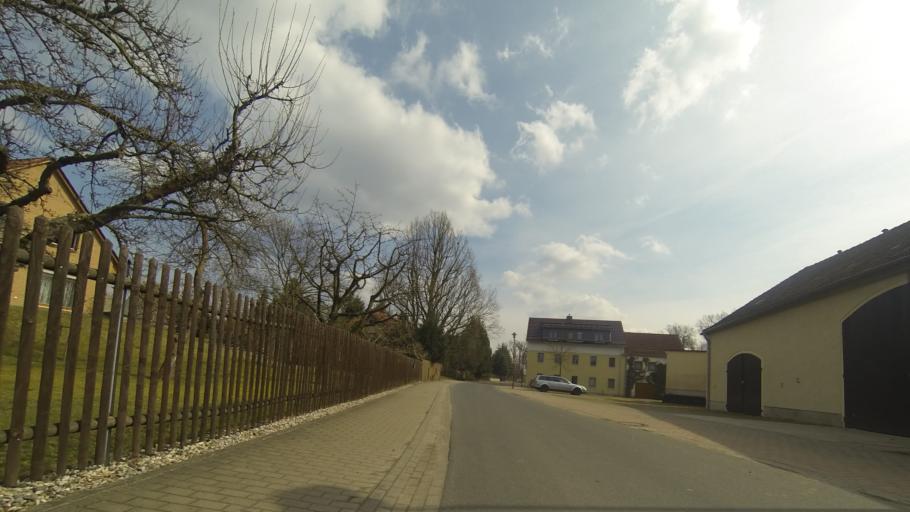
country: DE
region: Saxony
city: Radeburg
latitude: 51.2119
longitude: 13.7247
